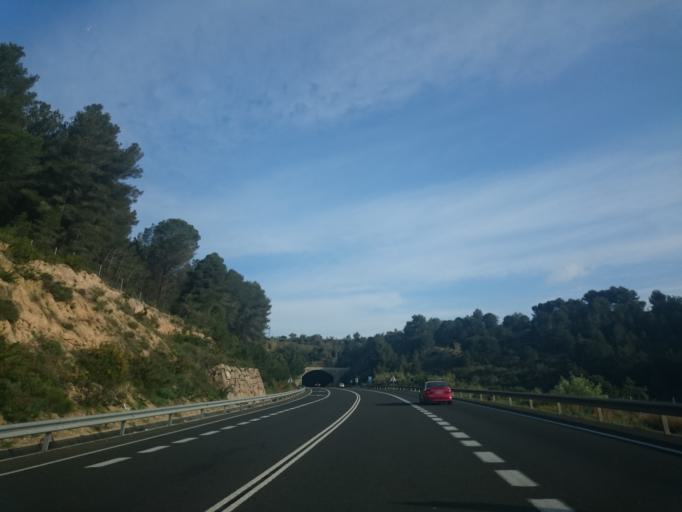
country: ES
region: Catalonia
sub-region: Provincia de Barcelona
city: Sant Pere de Riudebitlles
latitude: 41.4649
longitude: 1.6956
